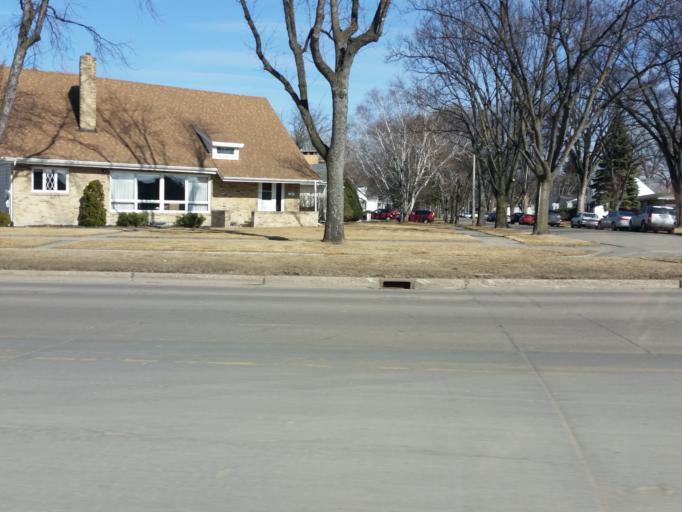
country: US
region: North Dakota
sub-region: Grand Forks County
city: Grand Forks
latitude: 47.9244
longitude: -97.0666
